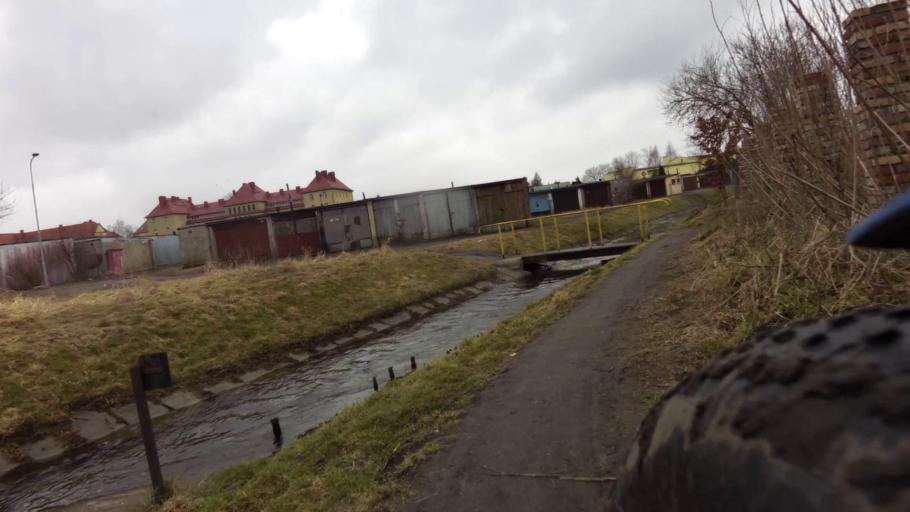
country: PL
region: West Pomeranian Voivodeship
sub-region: Powiat walecki
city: Walcz
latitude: 53.2809
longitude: 16.4697
